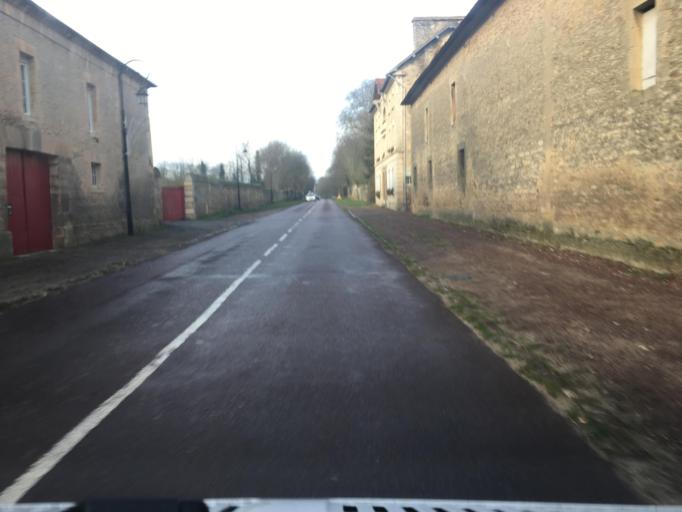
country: FR
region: Lower Normandy
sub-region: Departement du Calvados
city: Rots
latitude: 49.2011
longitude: -0.4814
